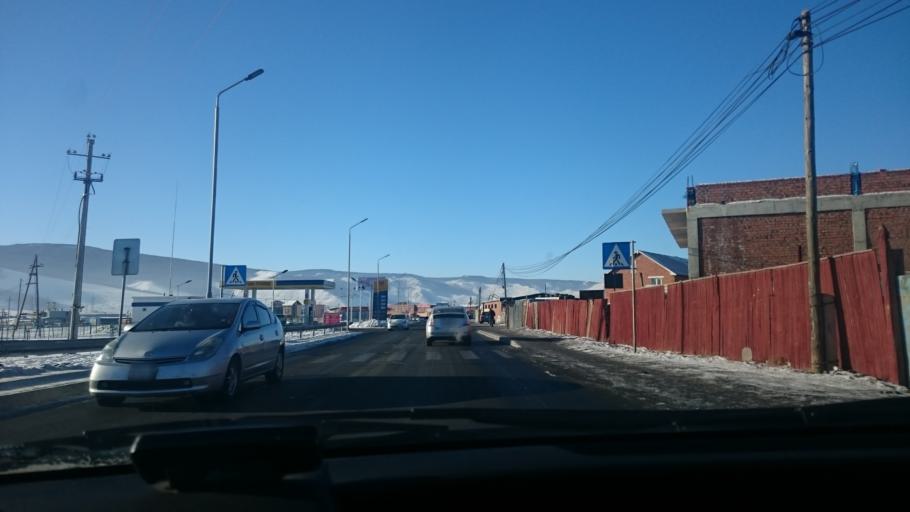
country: MN
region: Ulaanbaatar
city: Ulaanbaatar
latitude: 47.9084
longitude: 107.0367
